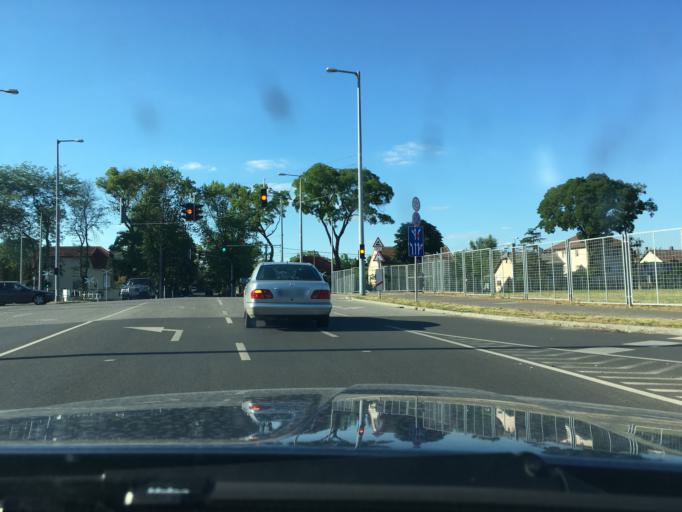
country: HU
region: Hajdu-Bihar
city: Debrecen
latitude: 47.5290
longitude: 21.6513
